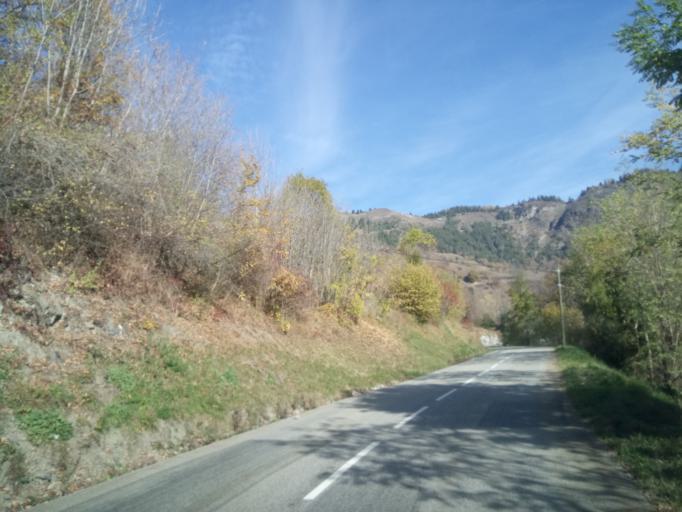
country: FR
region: Rhone-Alpes
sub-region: Departement de la Savoie
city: Saint-Jean-de-Maurienne
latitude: 45.2782
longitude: 6.3190
